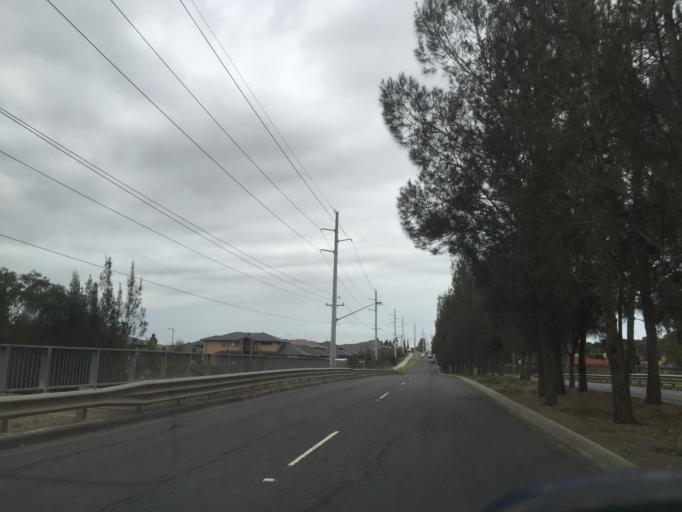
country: AU
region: New South Wales
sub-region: Blacktown
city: Doonside
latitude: -33.7836
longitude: 150.8725
